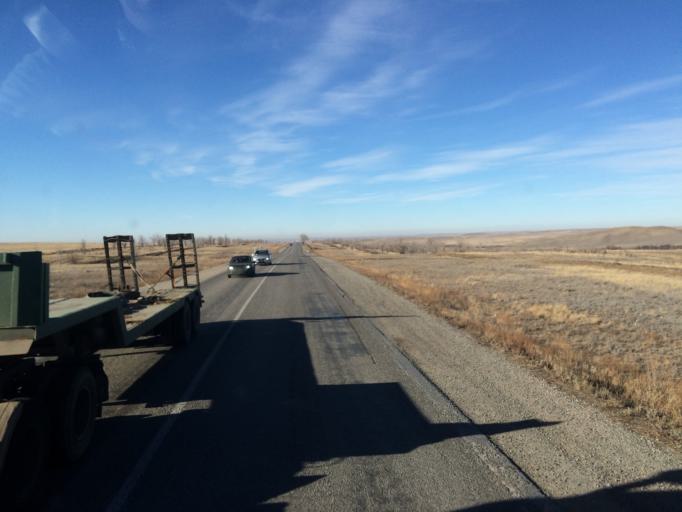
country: KZ
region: Aqtoebe
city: Aqtobe
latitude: 50.2820
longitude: 57.7461
